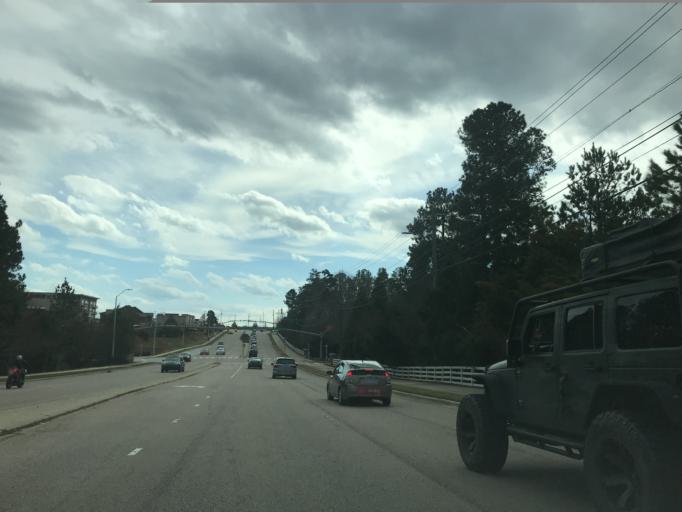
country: US
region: North Carolina
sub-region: Wake County
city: Morrisville
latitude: 35.7972
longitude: -78.8485
